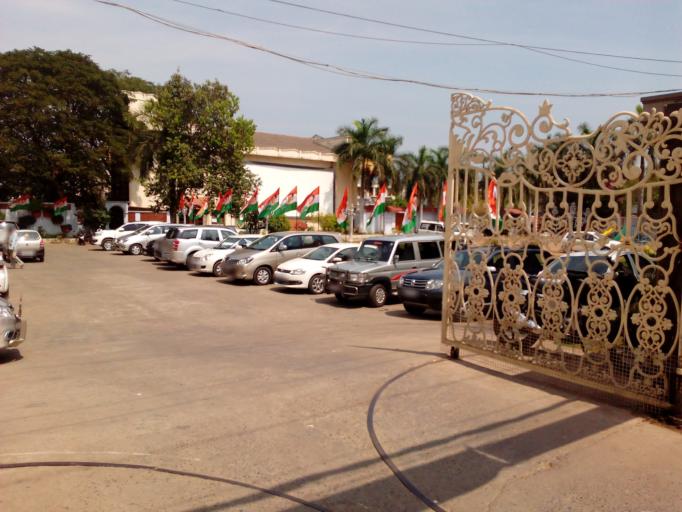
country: IN
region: Andhra Pradesh
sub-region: Krishna
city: Yanamalakuduru
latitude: 16.5054
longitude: 80.6606
